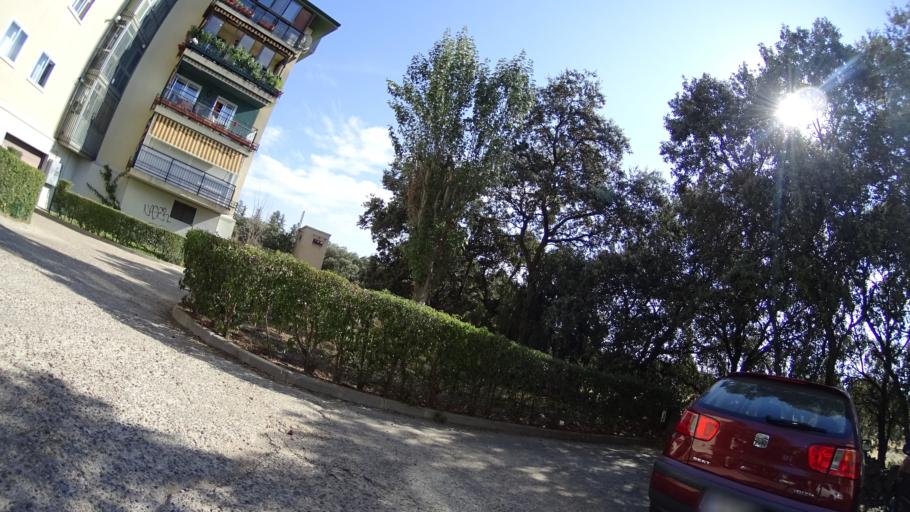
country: ES
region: Madrid
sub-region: Provincia de Madrid
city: Collado-Villalba
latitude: 40.6168
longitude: -4.0034
